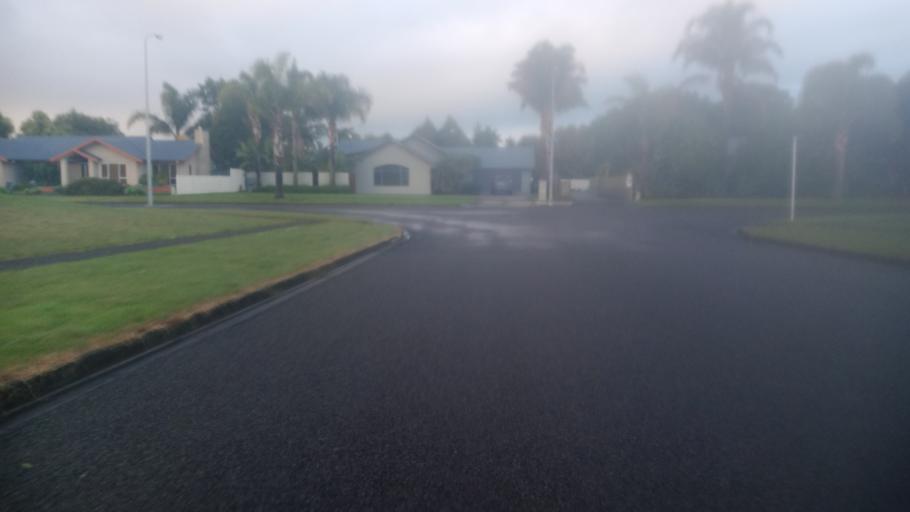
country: NZ
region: Gisborne
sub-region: Gisborne District
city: Gisborne
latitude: -38.6406
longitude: 177.9941
